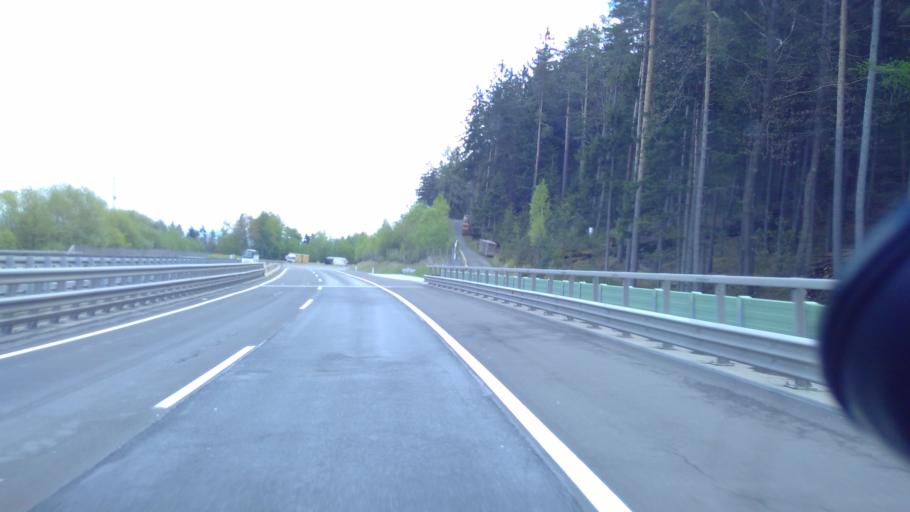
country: AT
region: Styria
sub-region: Politischer Bezirk Voitsberg
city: Ligist
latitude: 46.9745
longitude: 15.1904
